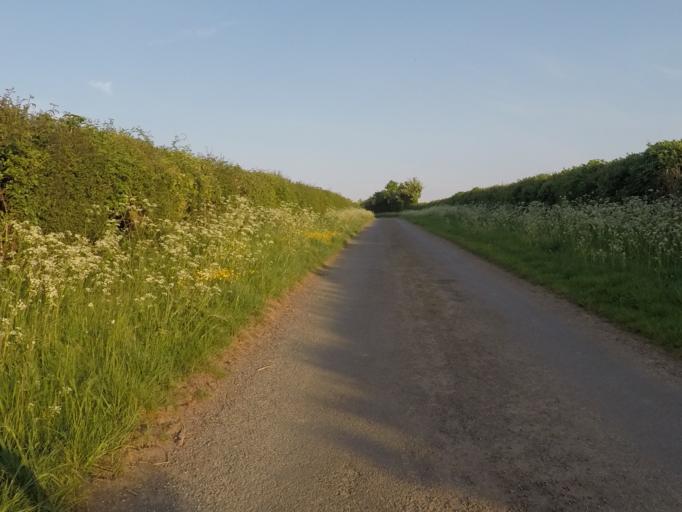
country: GB
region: England
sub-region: Oxfordshire
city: Shipton under Wychwood
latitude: 51.8582
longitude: -1.5528
